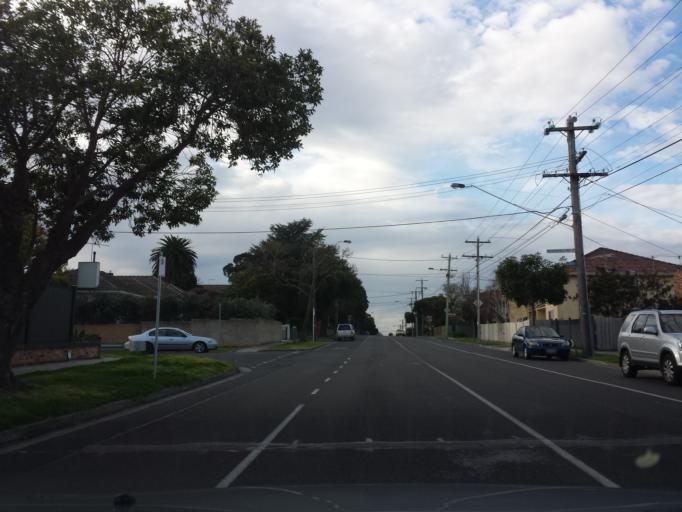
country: AU
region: Victoria
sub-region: Bayside
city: Cheltenham
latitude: -37.9728
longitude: 145.0543
